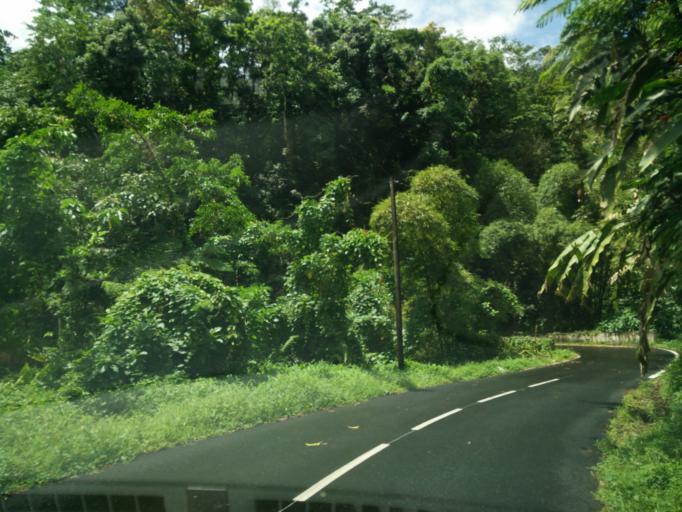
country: MQ
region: Martinique
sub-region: Martinique
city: Le Morne-Rouge
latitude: 14.7321
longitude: -61.1245
